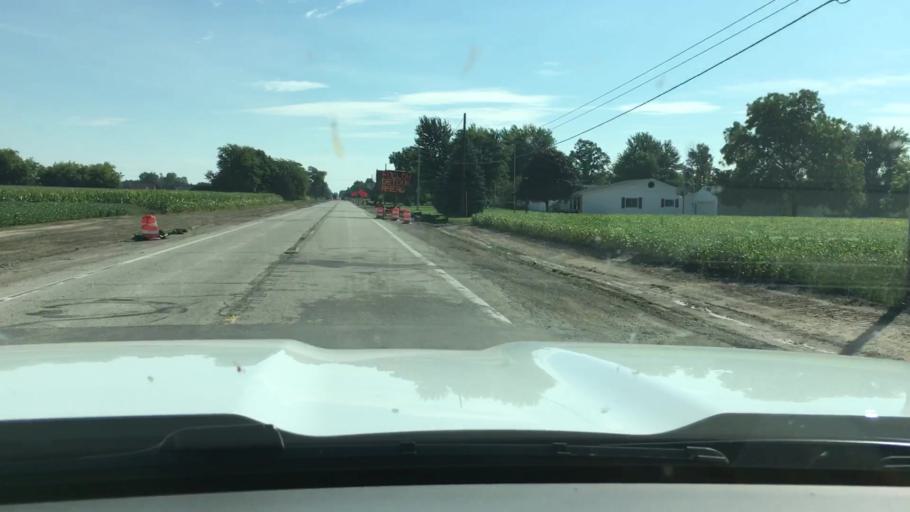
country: US
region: Michigan
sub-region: Saginaw County
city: Hemlock
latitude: 43.4125
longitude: -84.2748
